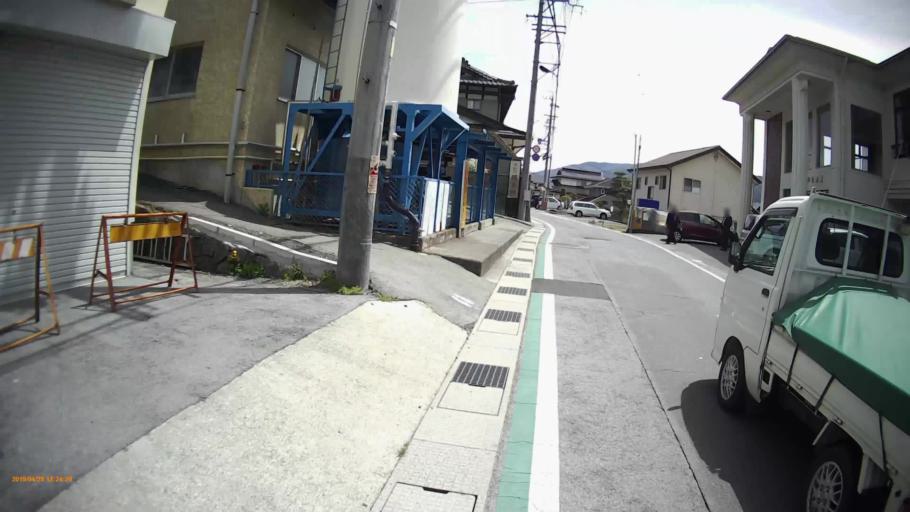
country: JP
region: Nagano
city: Chino
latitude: 36.0136
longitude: 138.1396
